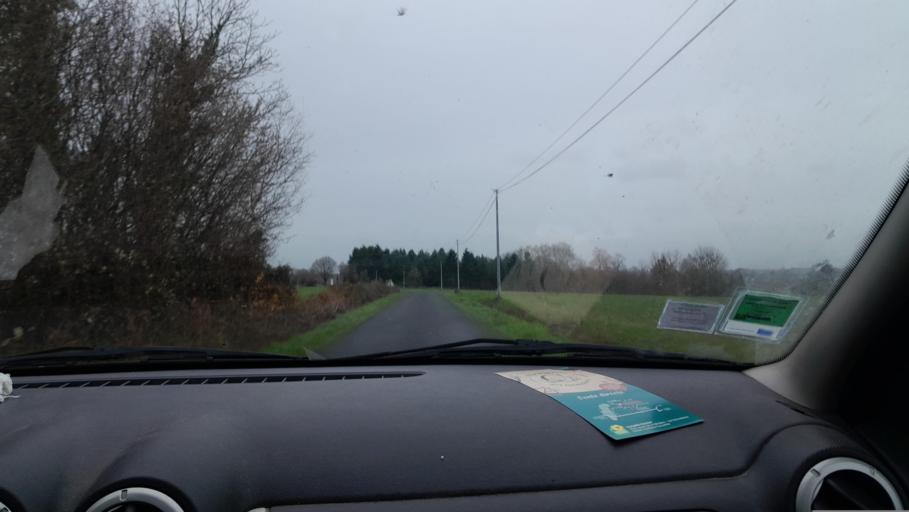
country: FR
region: Brittany
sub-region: Departement d'Ille-et-Vilaine
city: La Guerche-de-Bretagne
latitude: 47.9135
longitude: -1.1547
